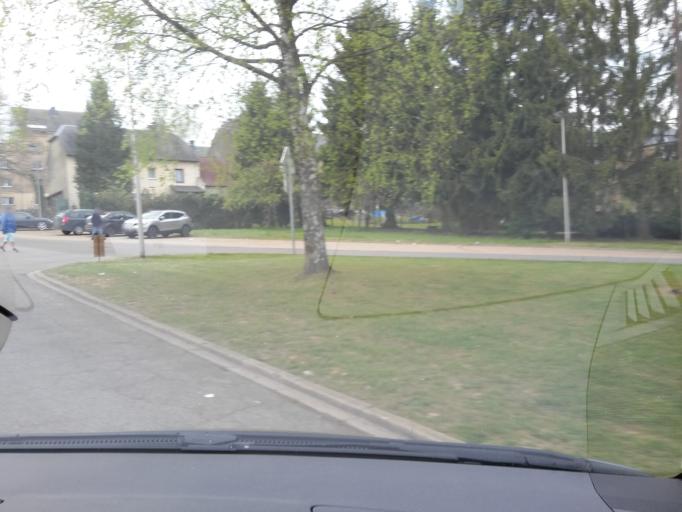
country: BE
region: Wallonia
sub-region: Province du Luxembourg
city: Messancy
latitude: 49.5989
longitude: 5.8138
